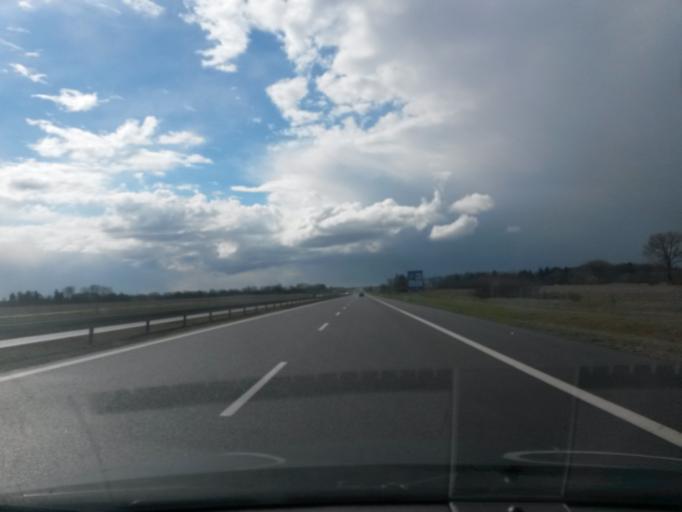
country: PL
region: Greater Poland Voivodeship
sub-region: Powiat wrzesinski
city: Wrzesnia
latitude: 52.3182
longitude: 17.5023
